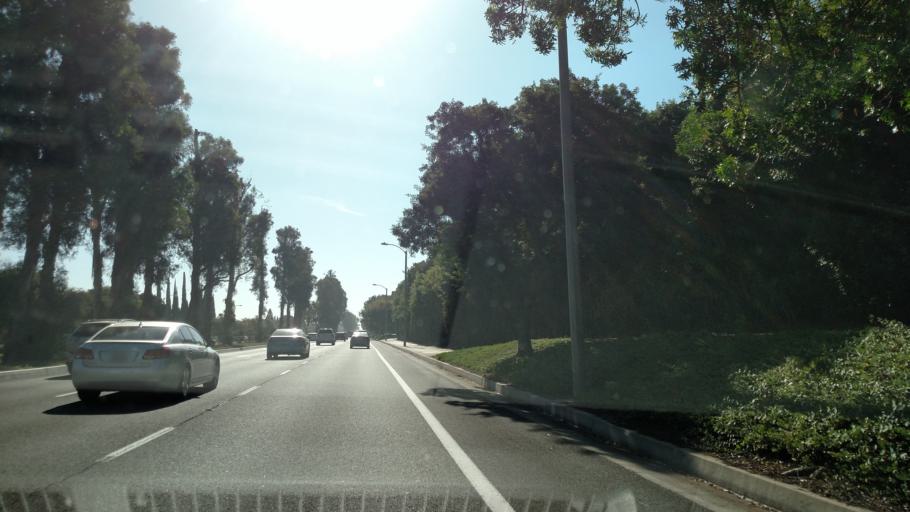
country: US
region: California
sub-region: Orange County
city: Irvine
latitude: 33.6852
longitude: -117.7871
